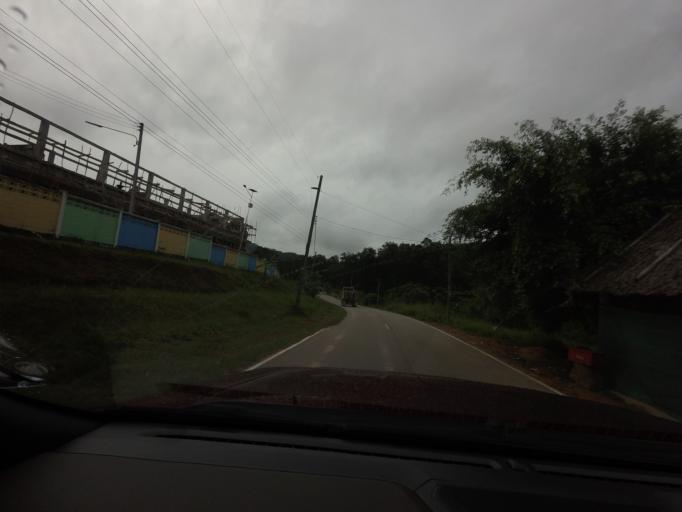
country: TH
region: Narathiwat
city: Chanae
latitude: 6.0273
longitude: 101.6962
